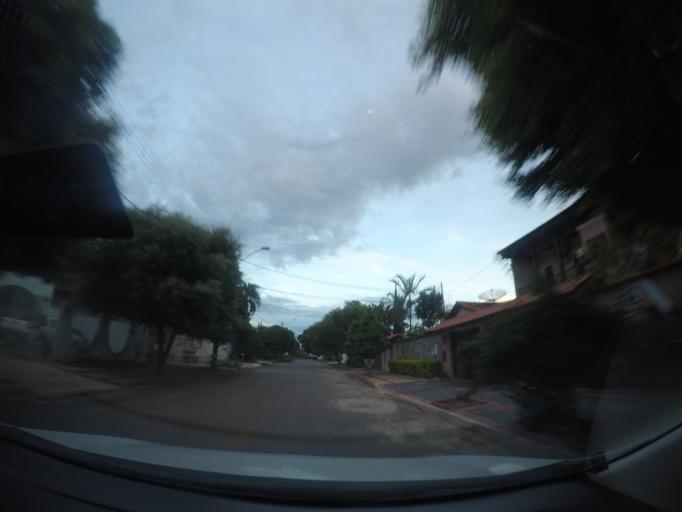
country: BR
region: Goias
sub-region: Goiania
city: Goiania
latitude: -16.6488
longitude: -49.2279
